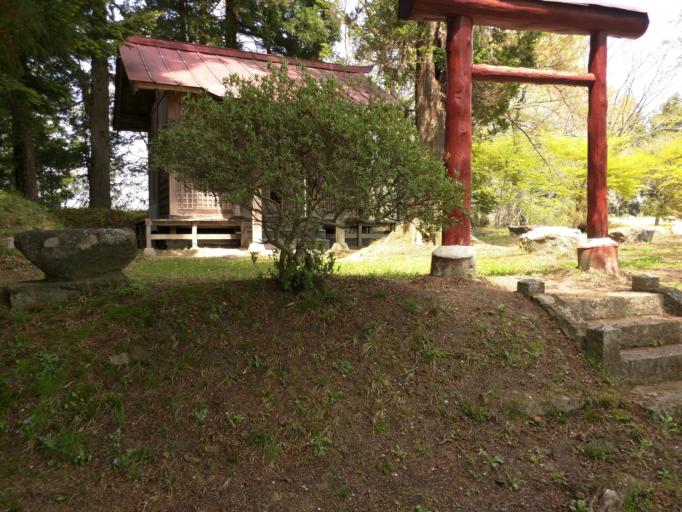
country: JP
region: Fukushima
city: Nihommatsu
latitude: 37.5472
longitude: 140.5057
